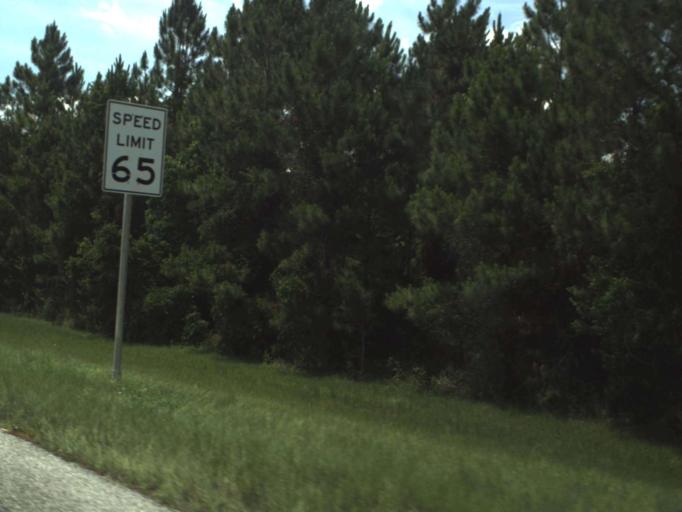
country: US
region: Florida
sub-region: Volusia County
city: Samsula-Spruce Creek
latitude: 29.0244
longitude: -81.1214
